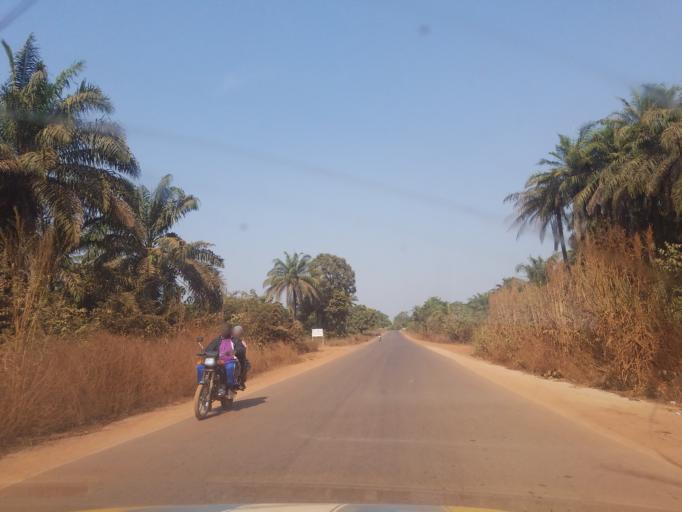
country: GN
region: Boke
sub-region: Boke Prefecture
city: Sangueya
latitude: 10.8279
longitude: -14.3692
